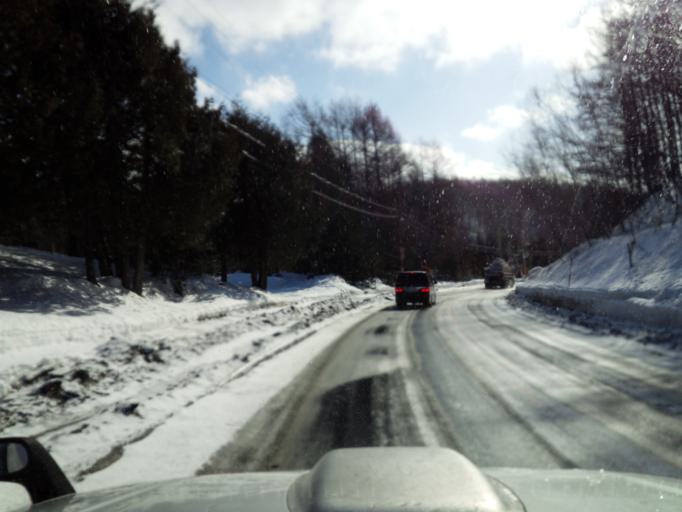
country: JP
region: Hokkaido
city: Sapporo
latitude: 42.9293
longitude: 141.3492
